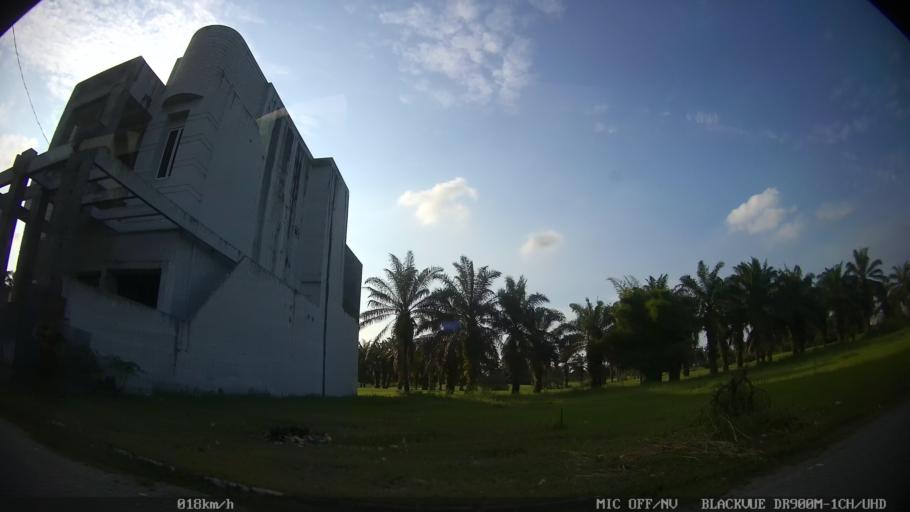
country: ID
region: North Sumatra
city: Medan
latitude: 3.6226
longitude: 98.6486
